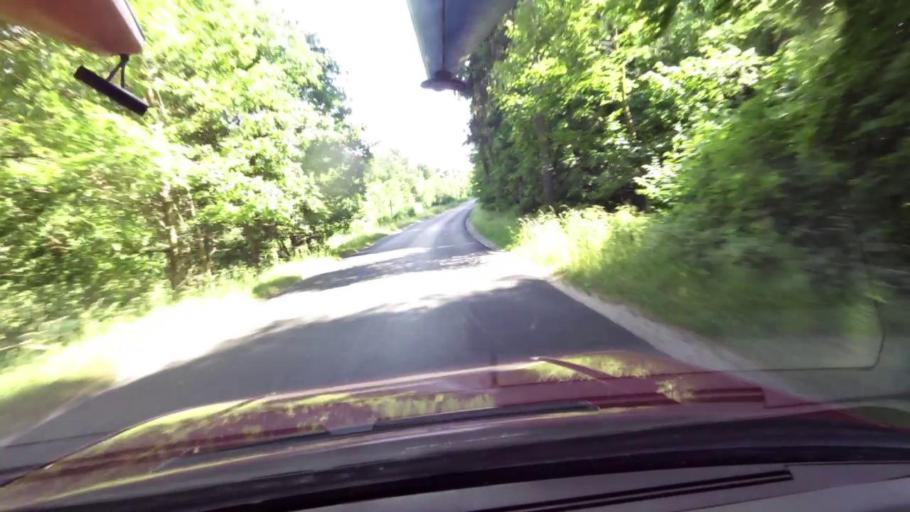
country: PL
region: Pomeranian Voivodeship
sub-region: Powiat slupski
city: Kepice
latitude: 54.2011
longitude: 16.8878
